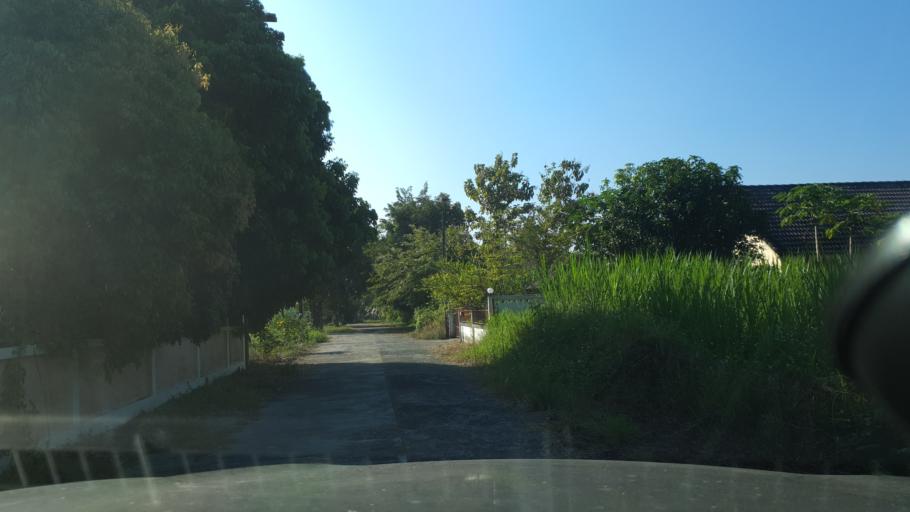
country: TH
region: Chiang Mai
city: San Kamphaeng
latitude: 18.7387
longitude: 99.1823
